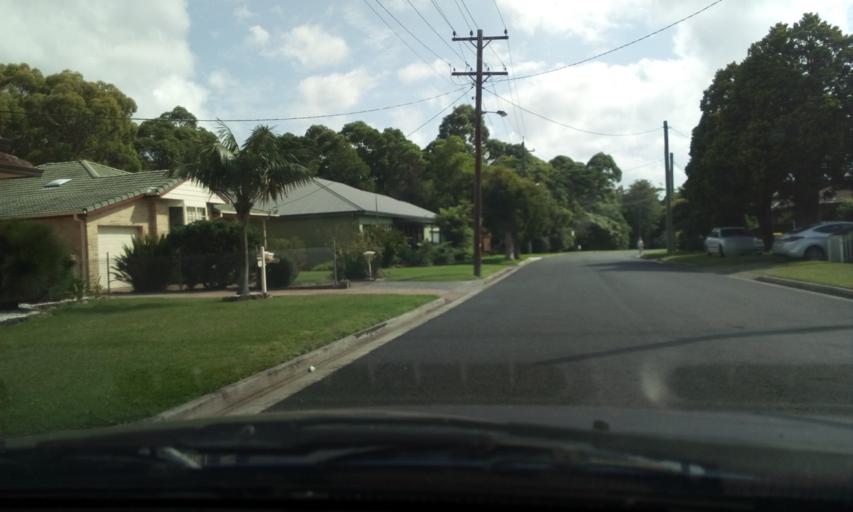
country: AU
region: New South Wales
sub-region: Wollongong
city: Corrimal
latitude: -34.3817
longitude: 150.8943
